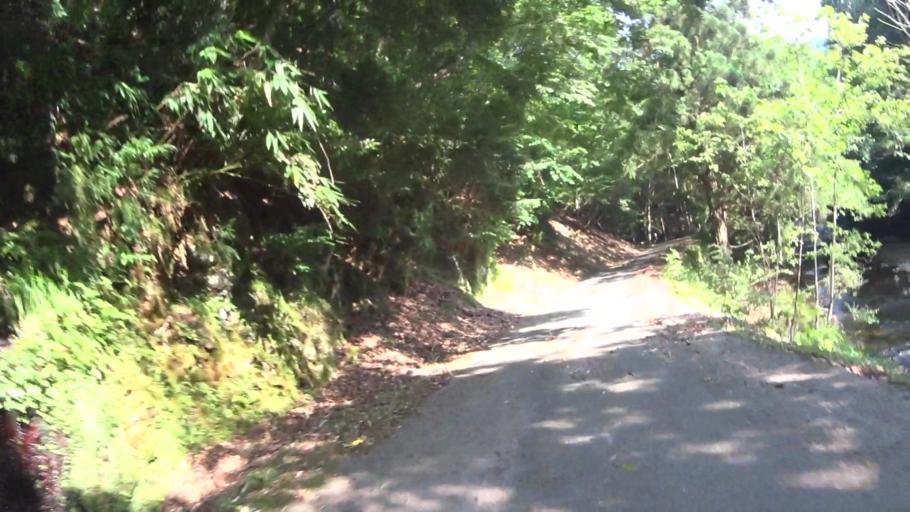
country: JP
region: Fukui
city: Obama
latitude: 35.2705
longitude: 135.6944
